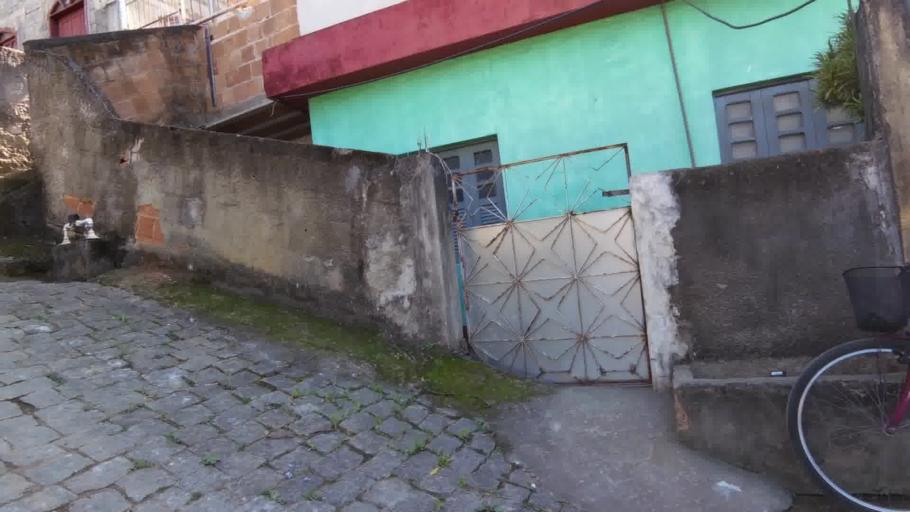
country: BR
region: Espirito Santo
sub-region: Rio Novo Do Sul
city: Rio Novo do Sul
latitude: -20.8620
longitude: -40.9308
